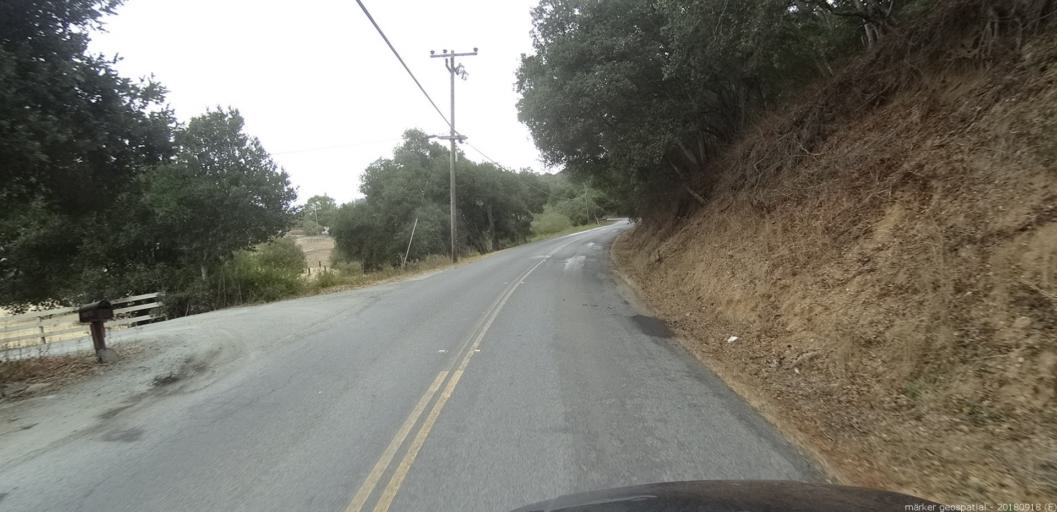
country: US
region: California
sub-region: Monterey County
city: Prunedale
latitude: 36.7785
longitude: -121.6482
